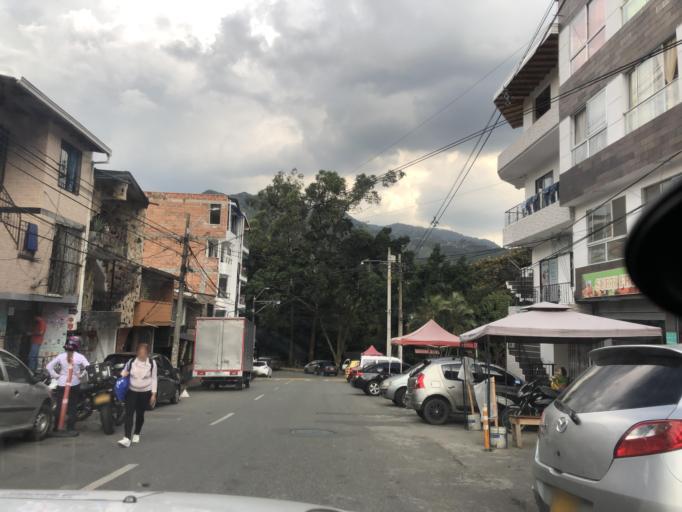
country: CO
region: Antioquia
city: Municipio de Copacabana
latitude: 6.3459
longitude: -75.5317
